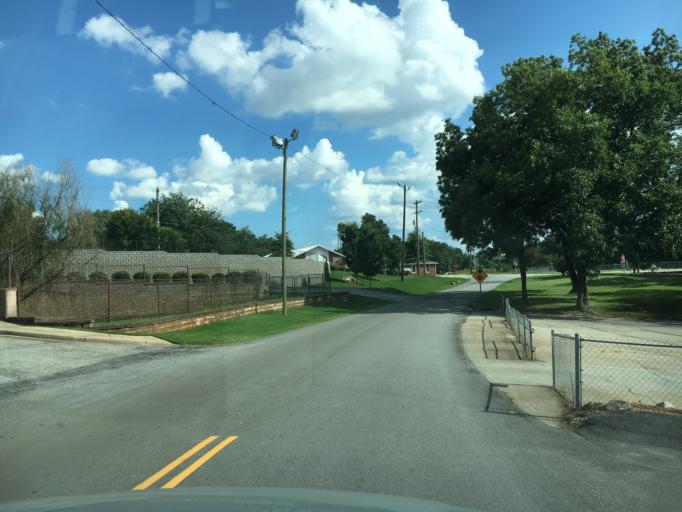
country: US
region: South Carolina
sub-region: Greenville County
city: Sans Souci
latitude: 34.8698
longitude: -82.4204
